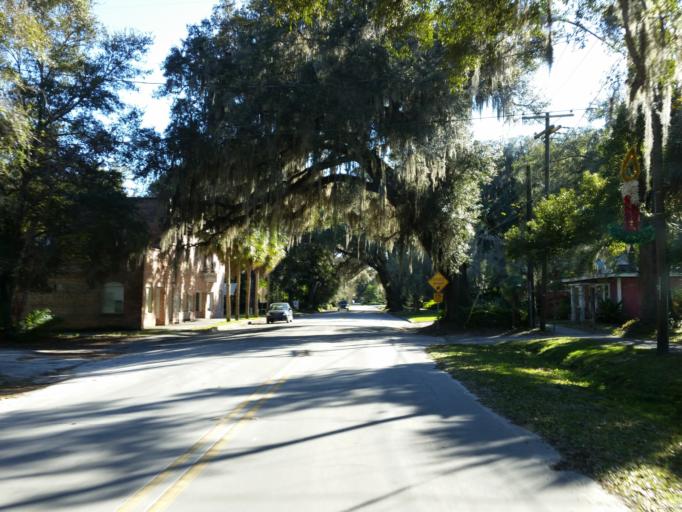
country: US
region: Florida
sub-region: Alachua County
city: Gainesville
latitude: 29.5077
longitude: -82.2795
